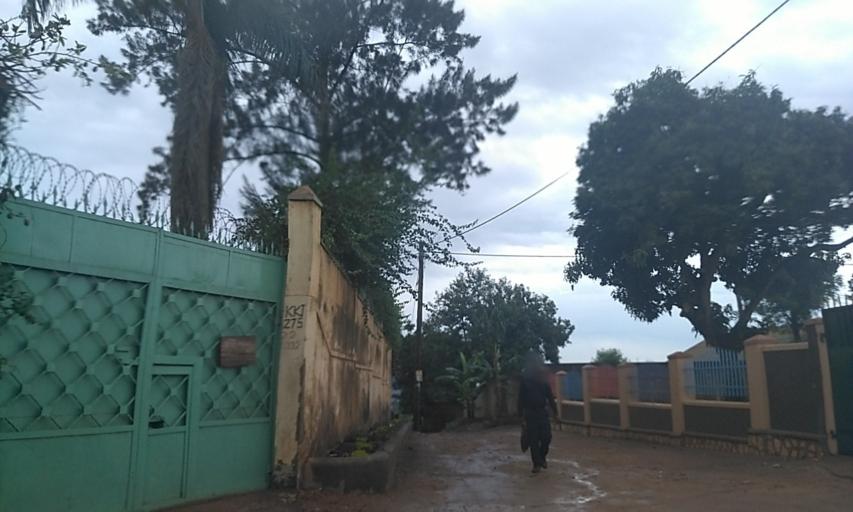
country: UG
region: Central Region
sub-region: Wakiso District
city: Bweyogerere
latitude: 0.3593
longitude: 32.6657
